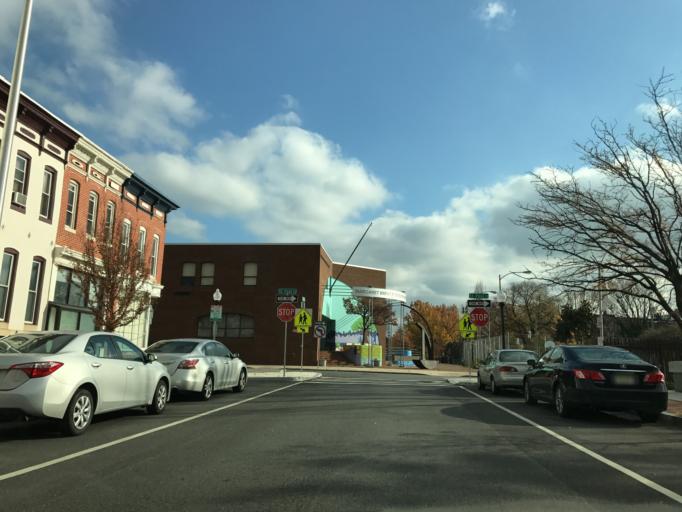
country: US
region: Maryland
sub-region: City of Baltimore
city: Baltimore
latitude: 39.3195
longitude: -76.6159
